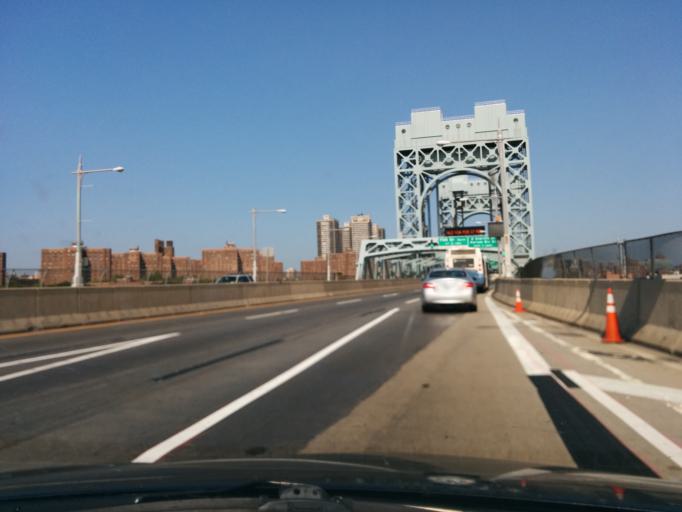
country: US
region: New York
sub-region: New York County
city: Manhattan
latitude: 40.7996
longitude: -73.9258
